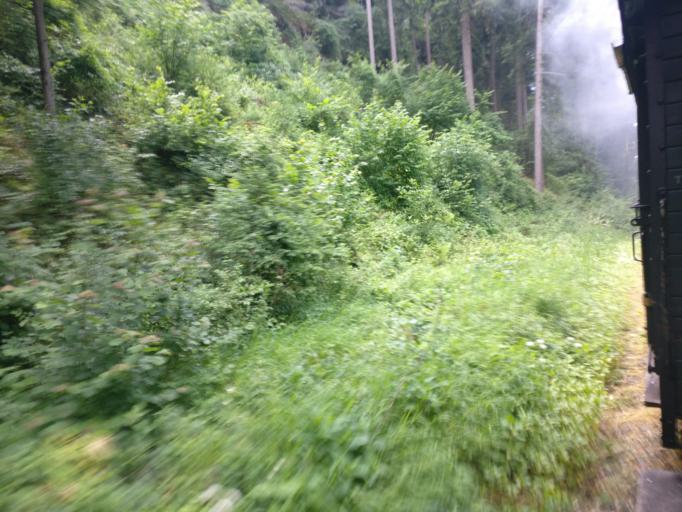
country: AT
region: Upper Austria
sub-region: Politischer Bezirk Steyr-Land
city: Waldneukirchen
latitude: 47.9997
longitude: 14.2855
